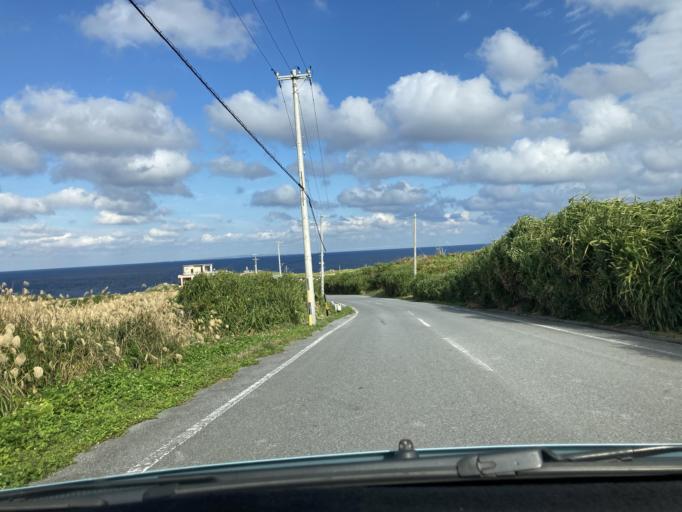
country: JP
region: Okinawa
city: Nago
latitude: 26.8709
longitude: 128.2617
